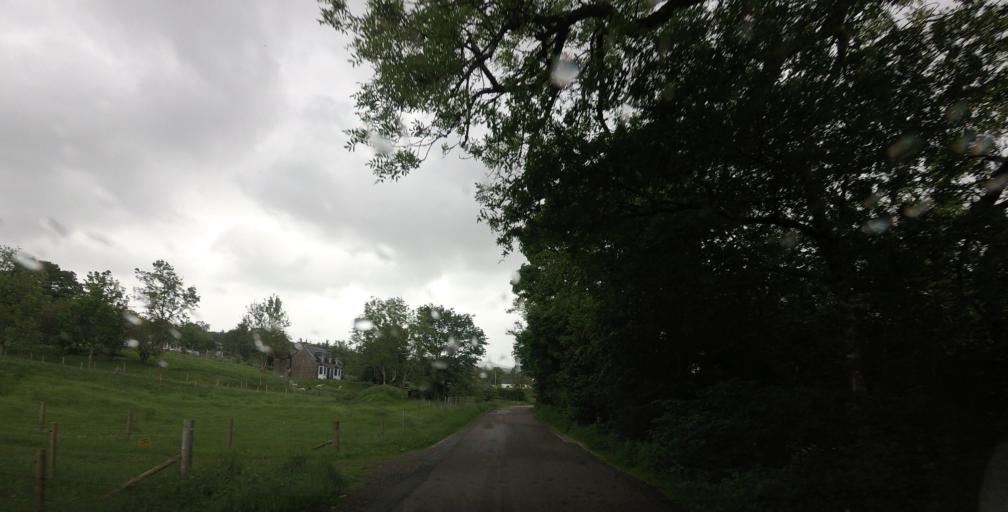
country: GB
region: Scotland
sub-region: Argyll and Bute
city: Oban
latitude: 56.7055
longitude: -5.5687
